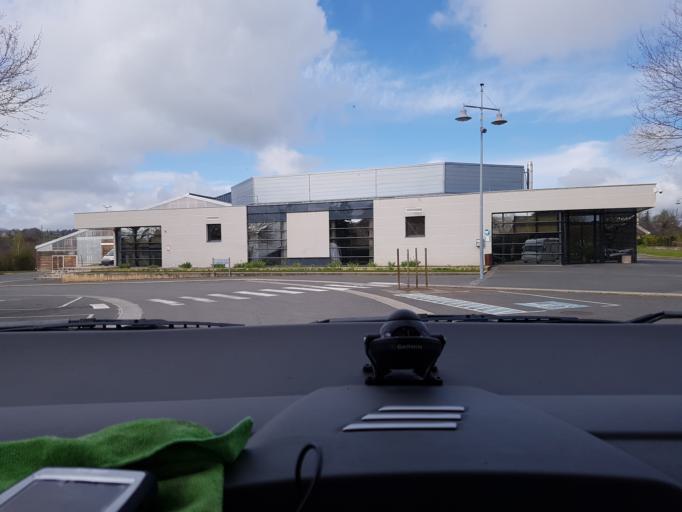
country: FR
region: Midi-Pyrenees
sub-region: Departement de l'Aveyron
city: Colombies
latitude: 44.4069
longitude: 2.2900
